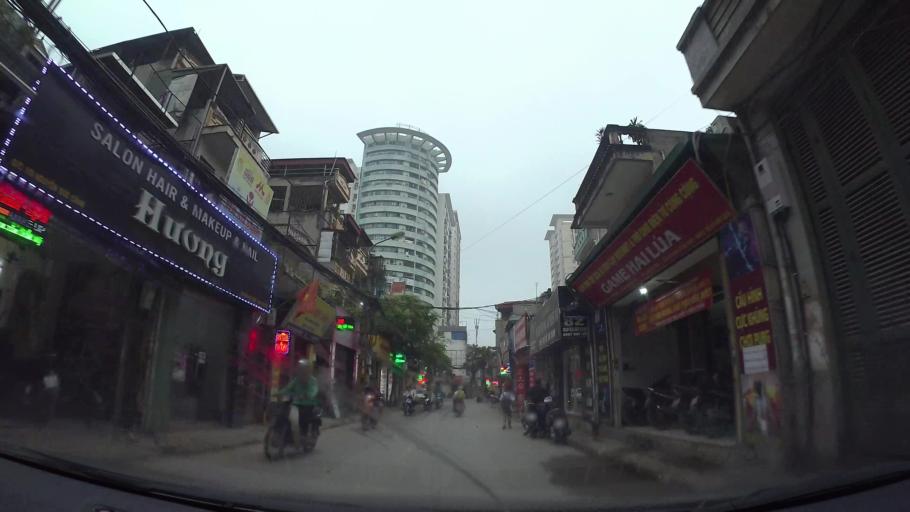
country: VN
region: Ha Noi
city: Hai BaTrung
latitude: 20.9872
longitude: 105.8505
